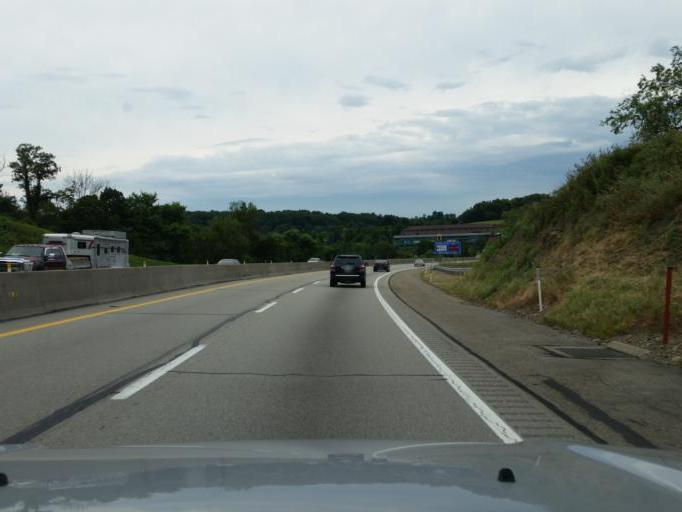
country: US
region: Pennsylvania
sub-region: Westmoreland County
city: Manor
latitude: 40.3190
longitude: -79.6791
